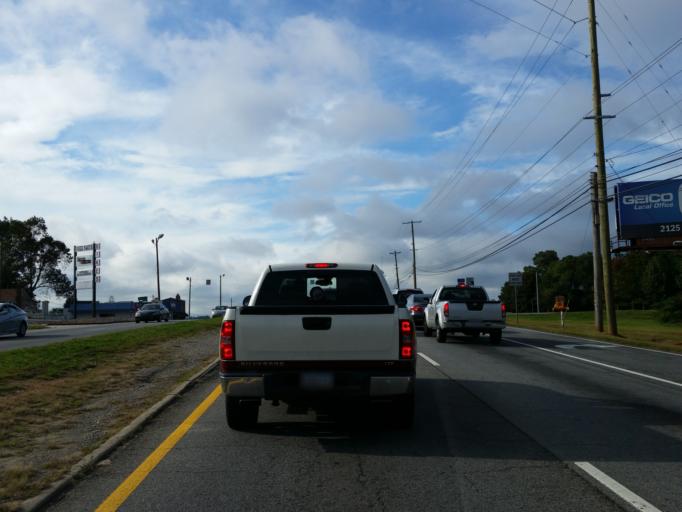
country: US
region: Georgia
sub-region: Cobb County
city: Marietta
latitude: 33.9588
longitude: -84.5264
